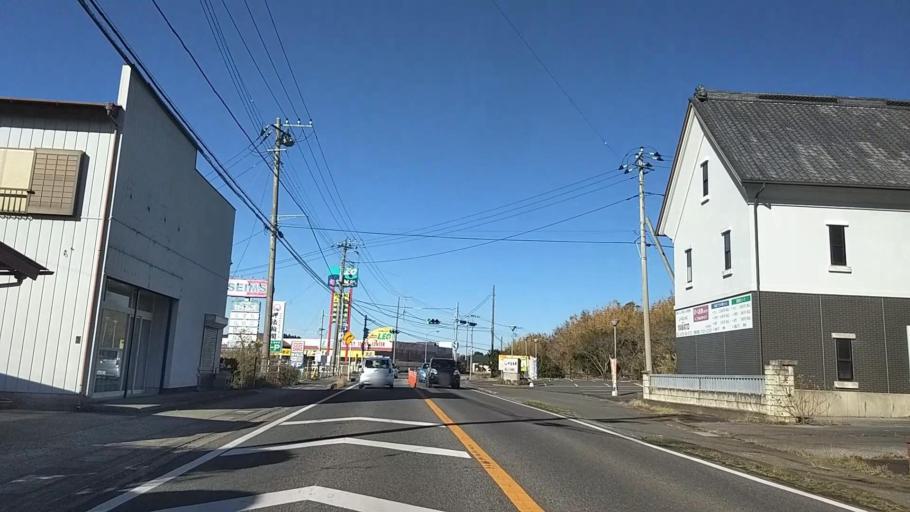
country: JP
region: Chiba
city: Ohara
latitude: 35.3146
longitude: 140.4022
